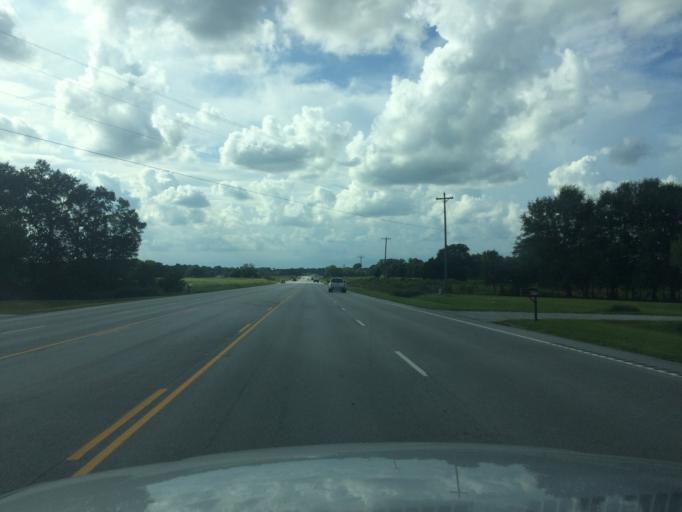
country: US
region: South Carolina
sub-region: Spartanburg County
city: Woodruff
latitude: 34.7969
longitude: -82.1175
